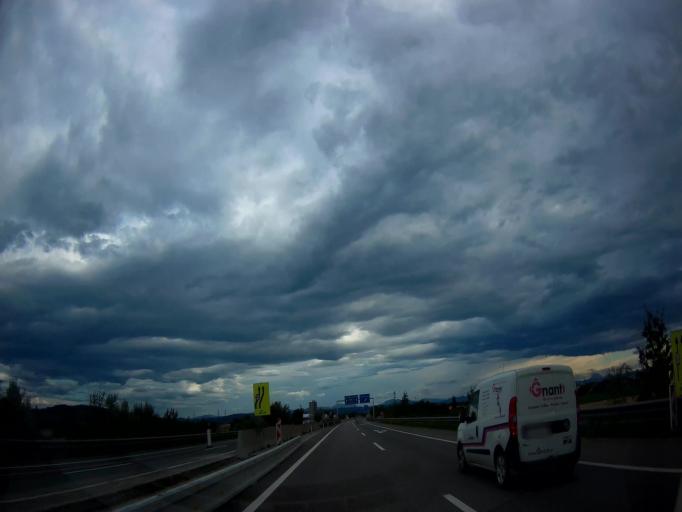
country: AT
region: Lower Austria
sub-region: Politischer Bezirk Sankt Polten
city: Herzogenburg
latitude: 48.2363
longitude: 15.6822
